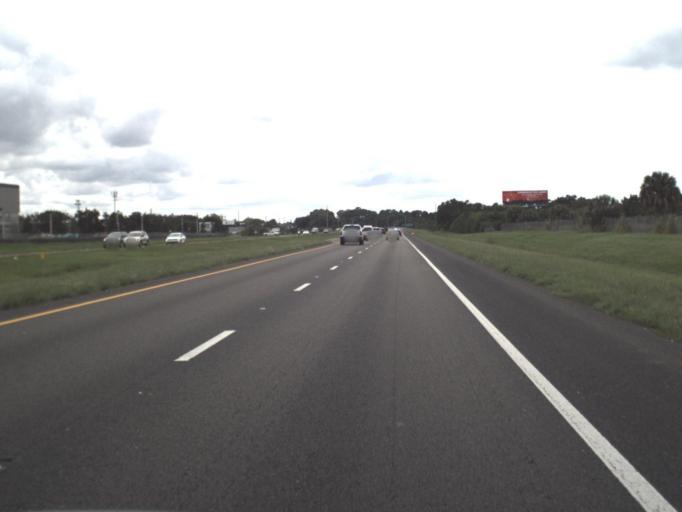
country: US
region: Florida
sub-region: Sarasota County
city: North Sarasota
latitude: 27.4001
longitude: -82.5331
